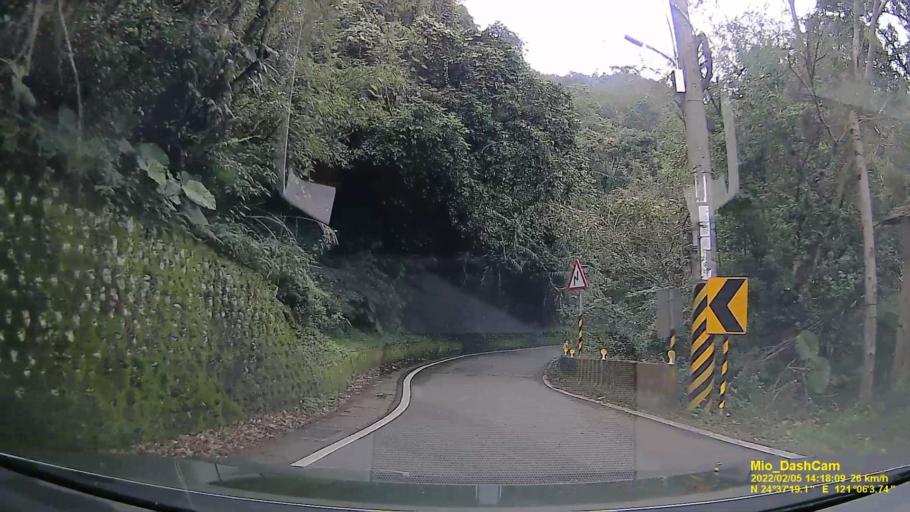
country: TW
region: Taiwan
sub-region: Hsinchu
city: Hsinchu
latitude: 24.6220
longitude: 121.1010
